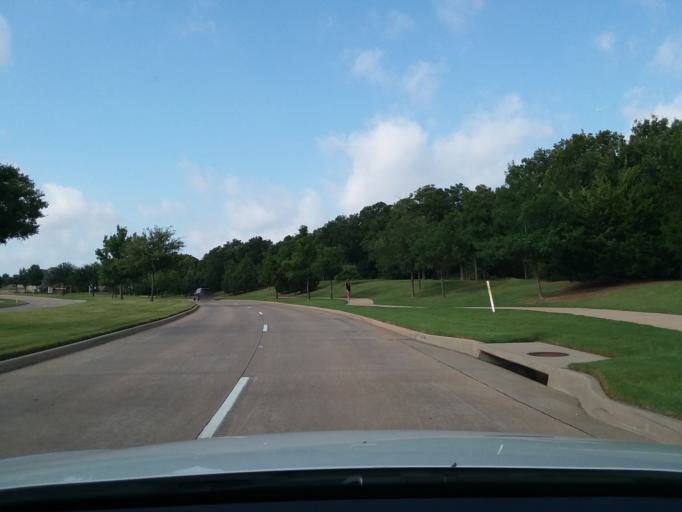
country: US
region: Texas
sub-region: Denton County
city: Copper Canyon
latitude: 33.1044
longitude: -97.1239
